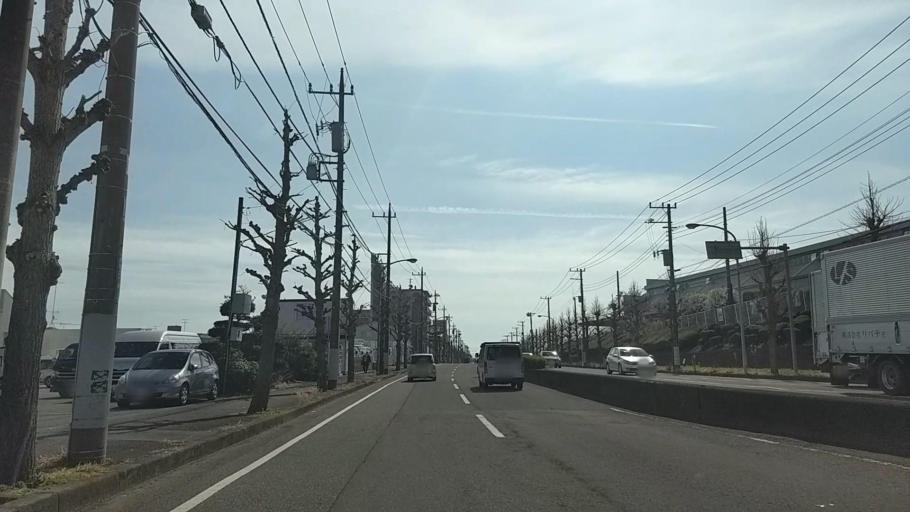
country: JP
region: Kanagawa
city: Fujisawa
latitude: 35.3936
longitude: 139.4578
